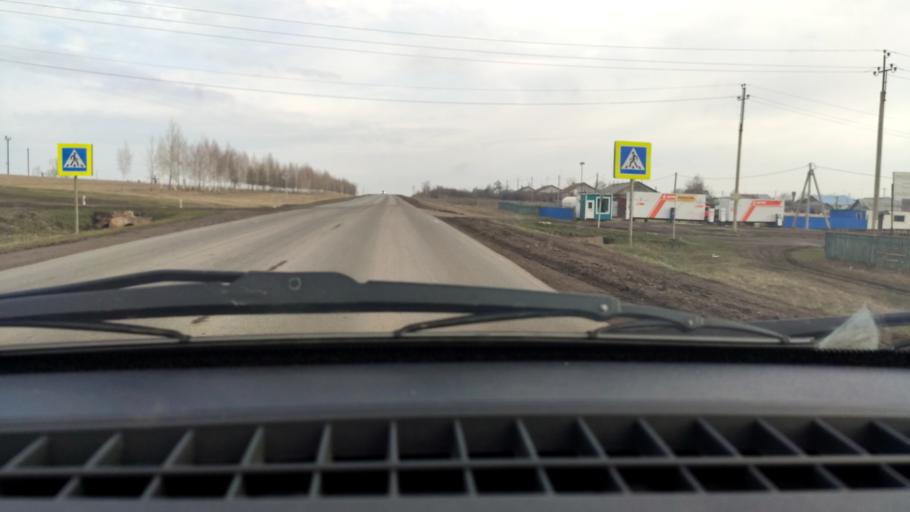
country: RU
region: Bashkortostan
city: Davlekanovo
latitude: 54.3712
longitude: 55.1954
